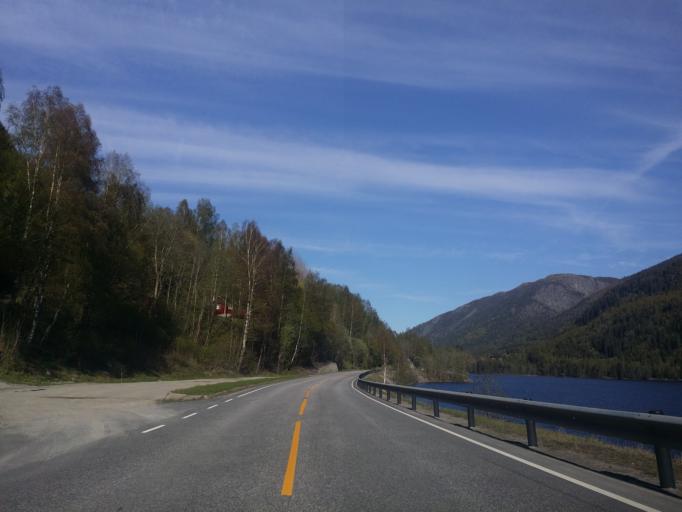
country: NO
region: Telemark
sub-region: Seljord
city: Seljord
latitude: 59.6054
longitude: 8.7252
